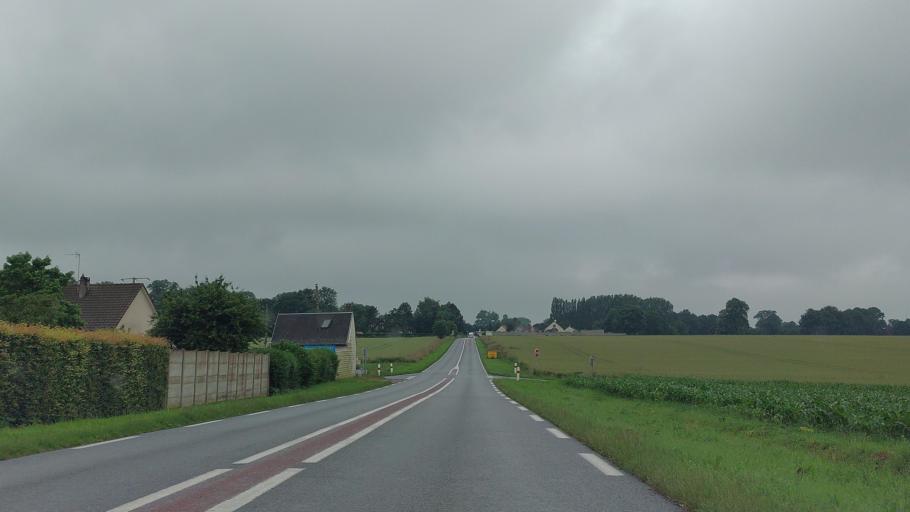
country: FR
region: Picardie
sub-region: Departement de la Somme
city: Chepy
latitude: 50.0816
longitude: 1.6365
